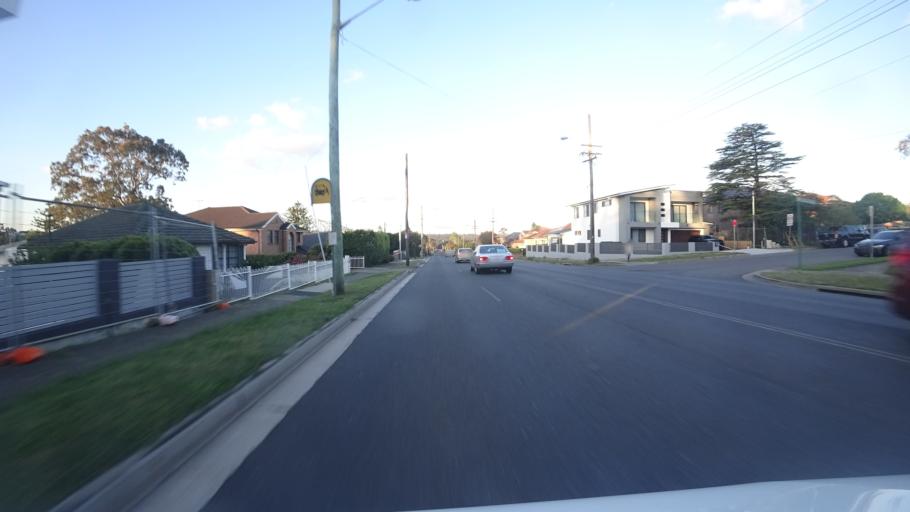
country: AU
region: New South Wales
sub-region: Ryde
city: North Ryde
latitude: -33.7960
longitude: 151.1251
